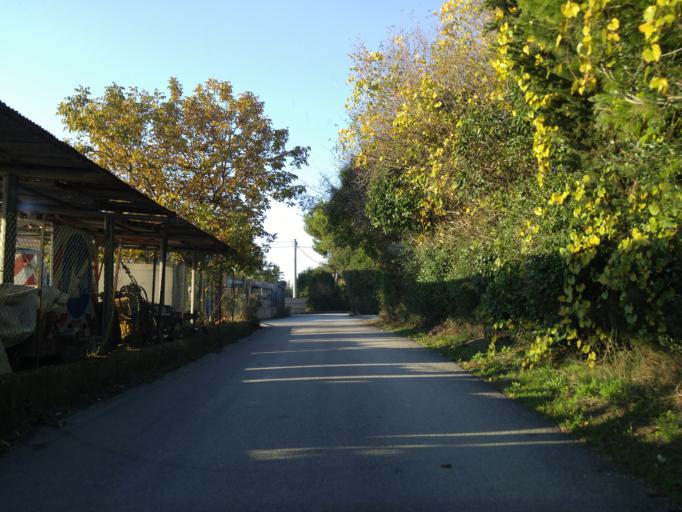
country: IT
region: The Marches
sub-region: Provincia di Pesaro e Urbino
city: Fano
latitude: 43.8140
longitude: 13.0323
